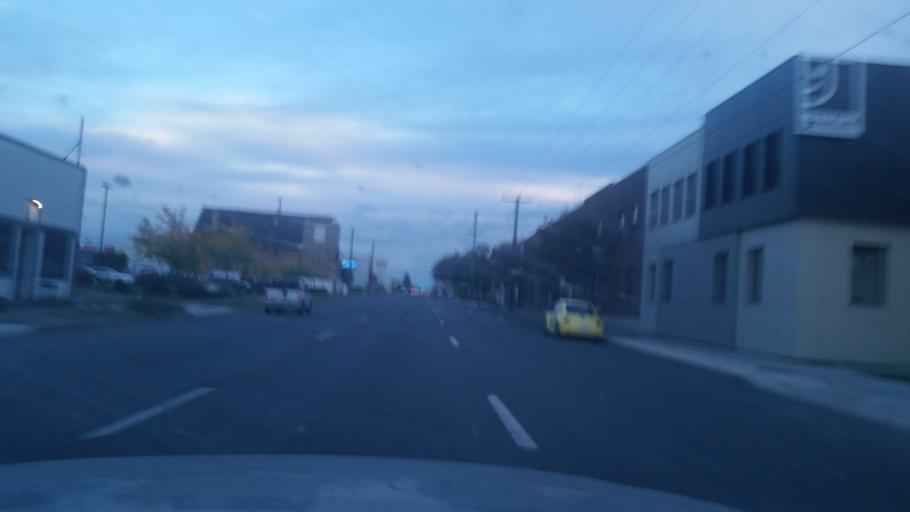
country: US
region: Washington
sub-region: Spokane County
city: Spokane
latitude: 47.6536
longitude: -117.4097
